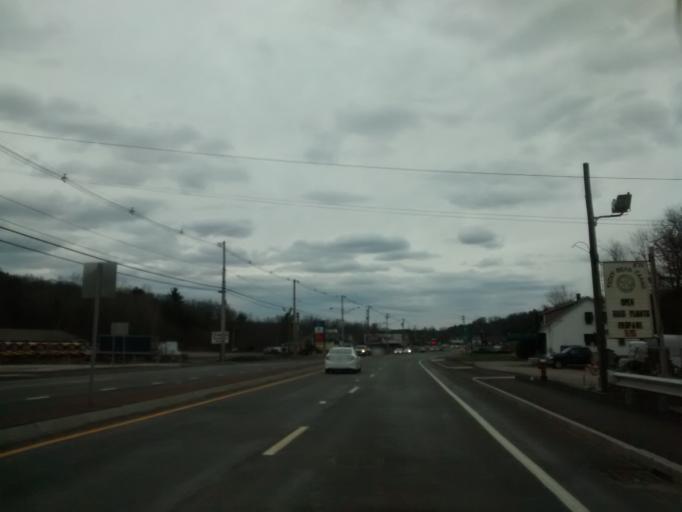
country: US
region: Massachusetts
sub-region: Worcester County
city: Auburn
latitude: 42.1766
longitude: -71.8740
